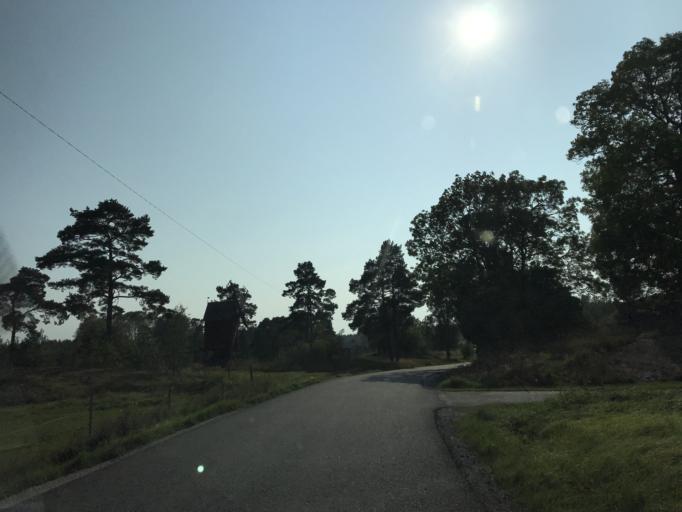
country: SE
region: Stockholm
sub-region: Norrtalje Kommun
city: Bjorko
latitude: 59.8571
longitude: 19.0230
